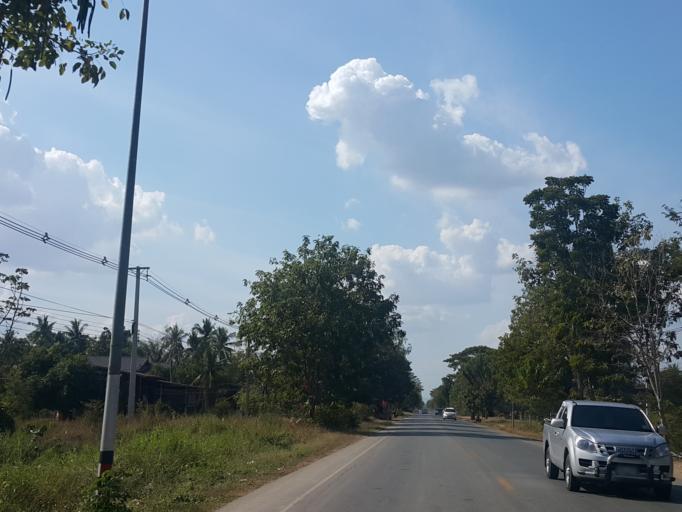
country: TH
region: Sukhothai
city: Sawankhalok
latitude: 17.3115
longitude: 99.7087
